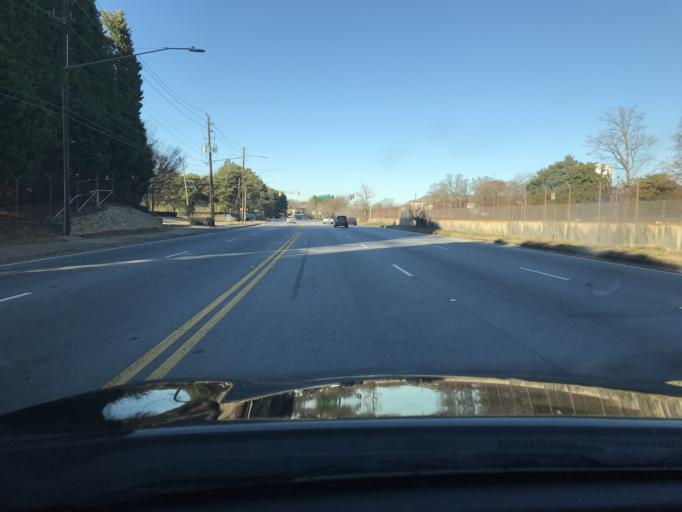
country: US
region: Georgia
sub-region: Fulton County
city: East Point
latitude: 33.7140
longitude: -84.4263
